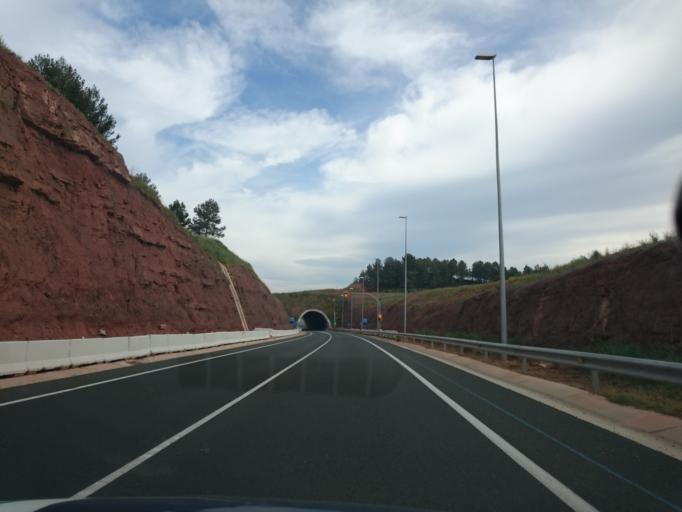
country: ES
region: Catalonia
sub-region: Provincia de Barcelona
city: Sant Salvador de Guardiola
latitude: 41.7113
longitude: 1.7845
